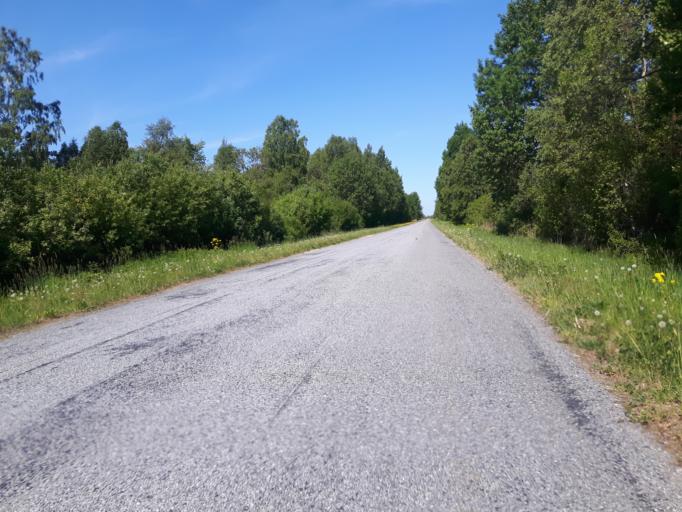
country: EE
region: Ida-Virumaa
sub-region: Aseri vald
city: Aseri
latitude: 59.4554
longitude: 26.8461
